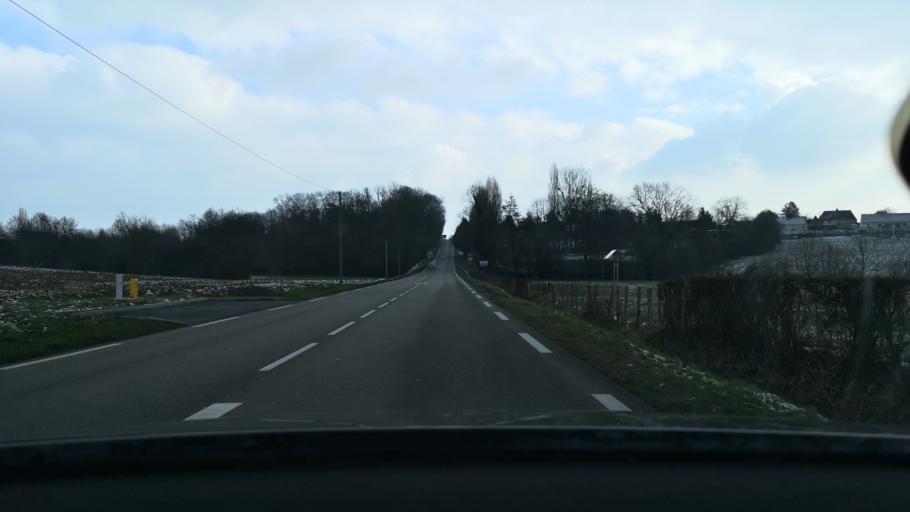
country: FR
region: Bourgogne
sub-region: Departement de Saone-et-Loire
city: Mervans
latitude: 46.7432
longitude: 5.1143
